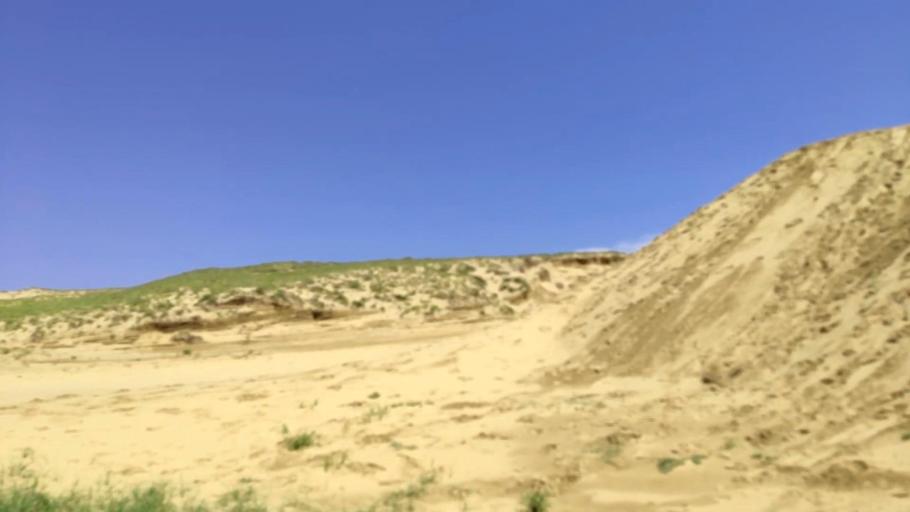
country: JP
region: Tottori
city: Tottori
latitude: 35.5424
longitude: 134.2326
